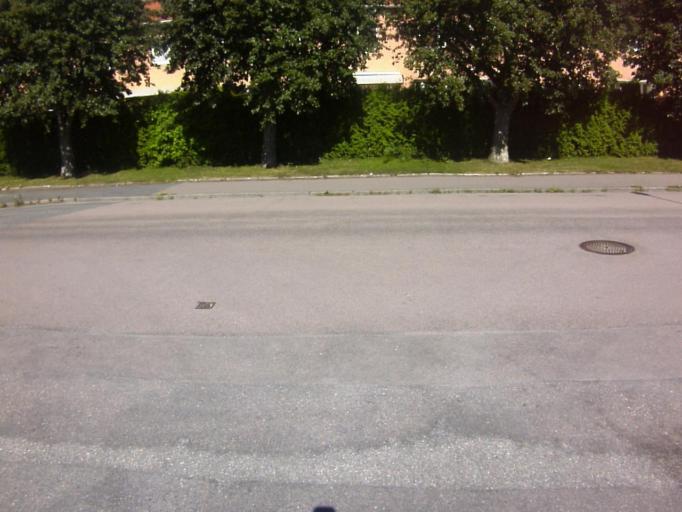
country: SE
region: Soedermanland
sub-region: Eskilstuna Kommun
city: Eskilstuna
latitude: 59.3721
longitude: 16.5383
